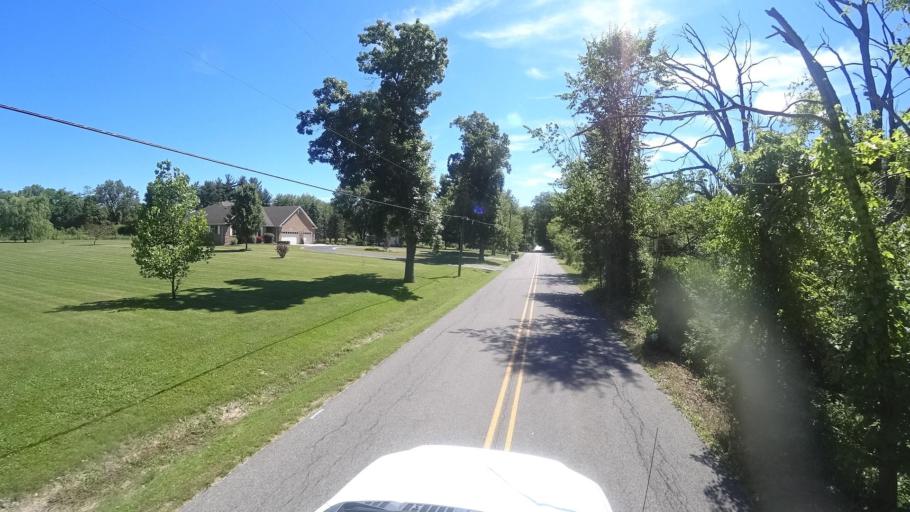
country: US
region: Indiana
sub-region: Porter County
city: Porter
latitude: 41.6296
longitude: -87.0805
